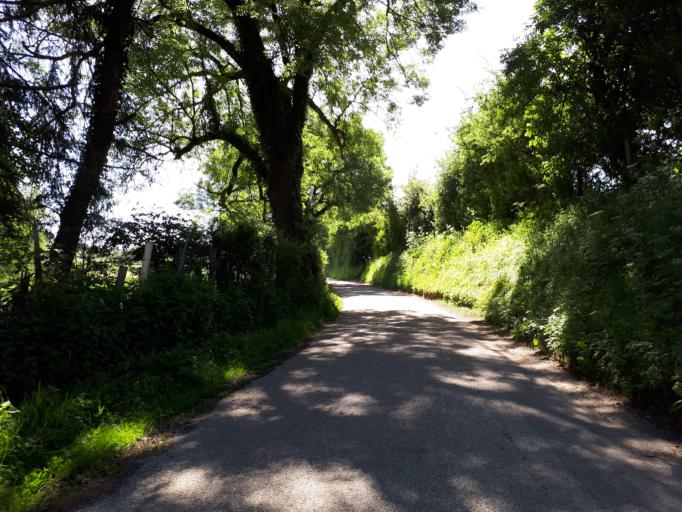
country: FR
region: Rhone-Alpes
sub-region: Departement de l'Isere
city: Saint-Savin
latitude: 45.6122
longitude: 5.3033
